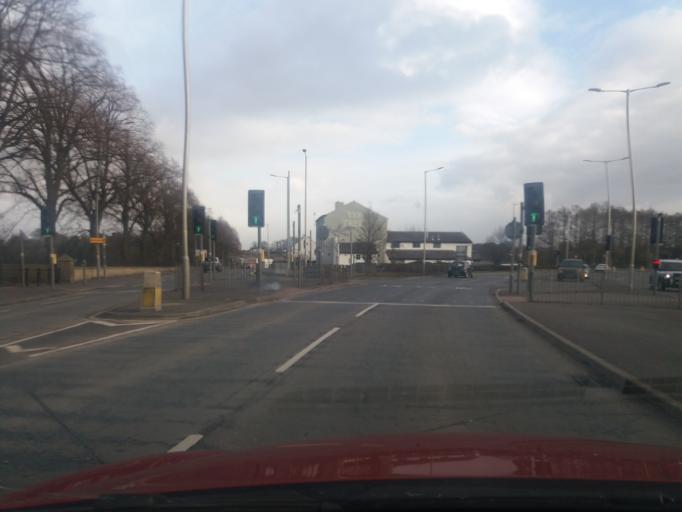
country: GB
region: England
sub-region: Lancashire
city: Preston
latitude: 53.7503
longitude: -2.6755
